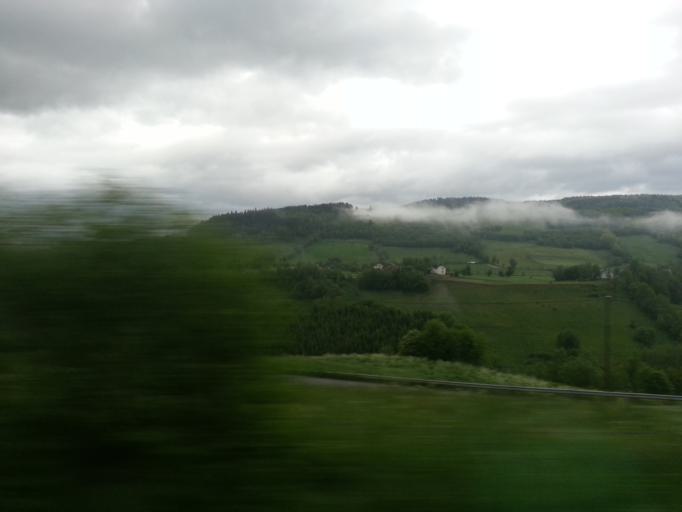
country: NO
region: Sor-Trondelag
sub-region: Midtre Gauldal
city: Storen
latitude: 62.9573
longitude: 10.1763
